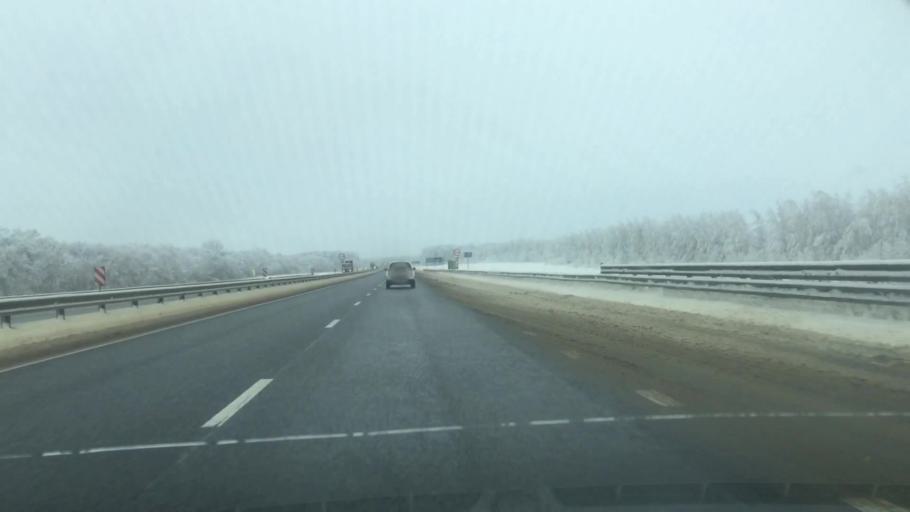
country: RU
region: Lipetsk
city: Zadonsk
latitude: 52.5007
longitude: 38.7553
